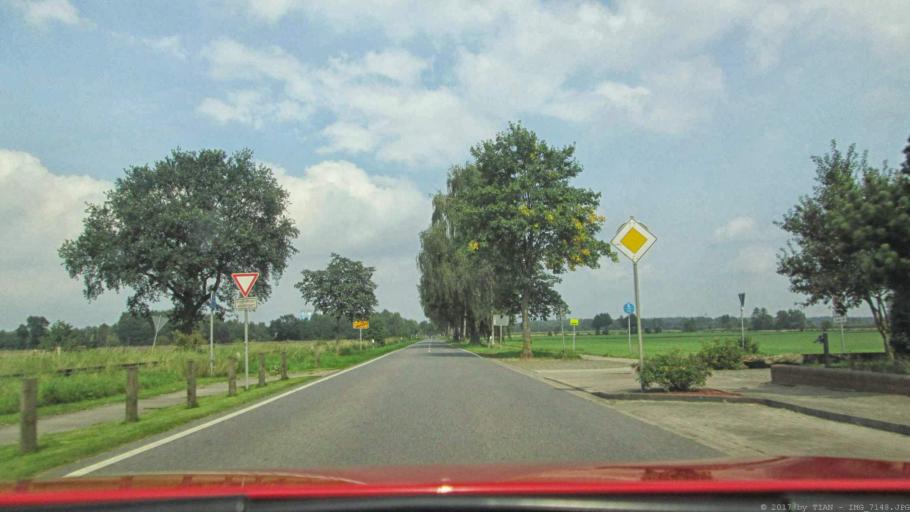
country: DE
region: Lower Saxony
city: Neetze
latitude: 53.2710
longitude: 10.6281
